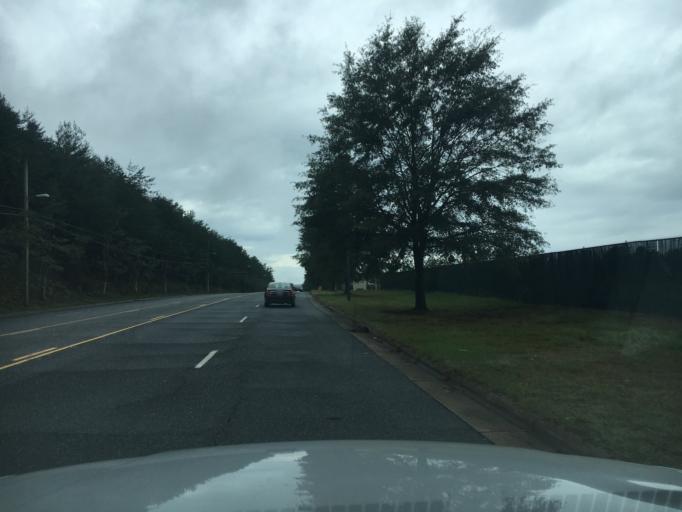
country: US
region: North Carolina
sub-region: Catawba County
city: Longview
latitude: 35.7474
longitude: -81.3683
